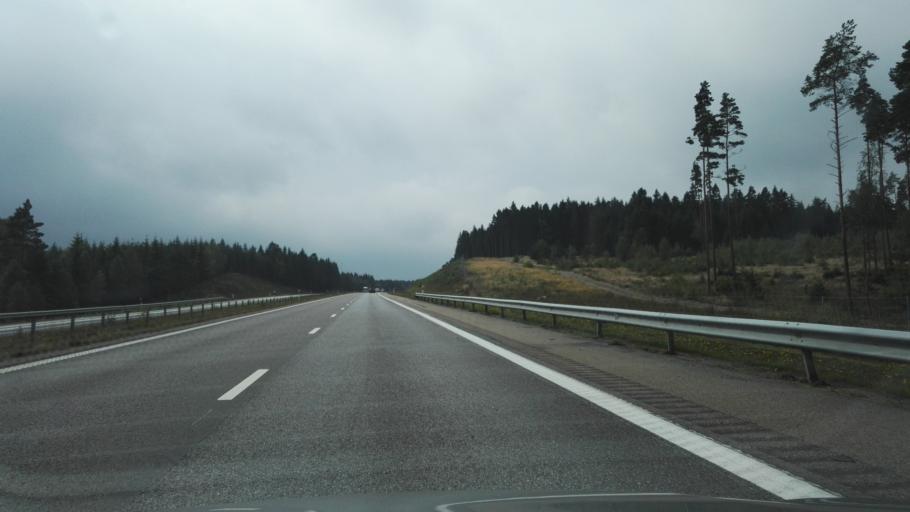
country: SE
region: Kronoberg
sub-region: Markaryds Kommun
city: Stromsnasbruk
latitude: 56.5983
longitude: 13.7388
